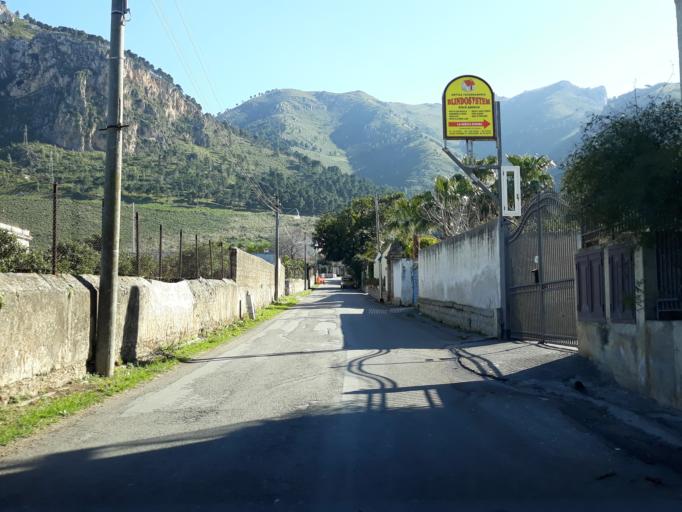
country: IT
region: Sicily
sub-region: Palermo
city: Villa Ciambra
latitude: 38.0784
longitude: 13.3468
